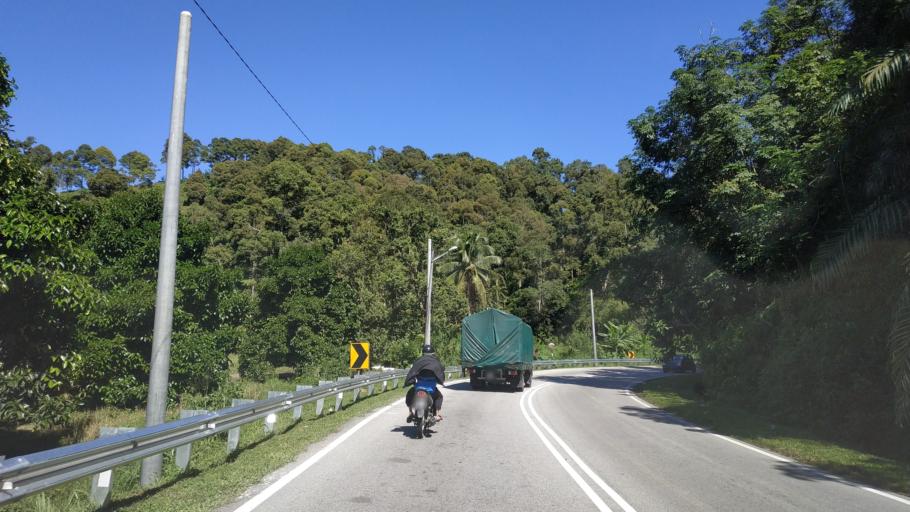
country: MY
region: Kedah
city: Kulim
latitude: 5.3274
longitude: 100.5320
